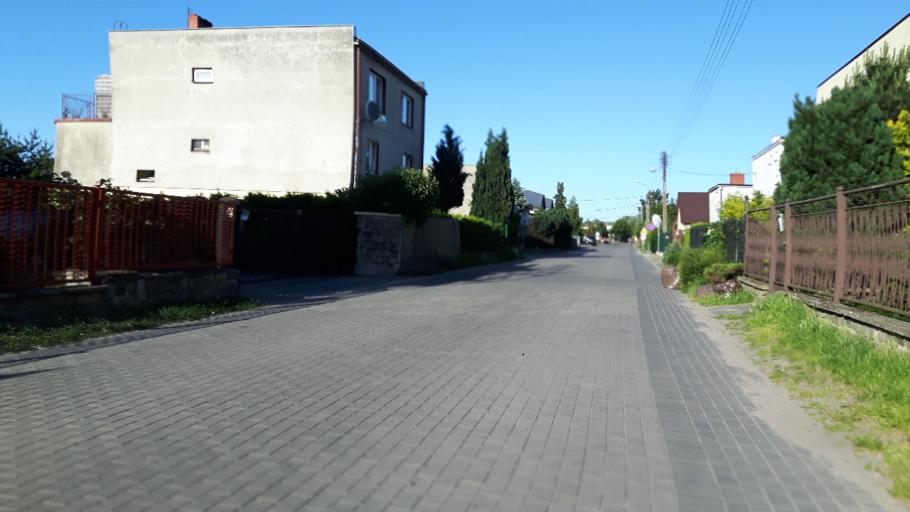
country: PL
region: Pomeranian Voivodeship
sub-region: Powiat pucki
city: Mosty
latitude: 54.6085
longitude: 18.4922
